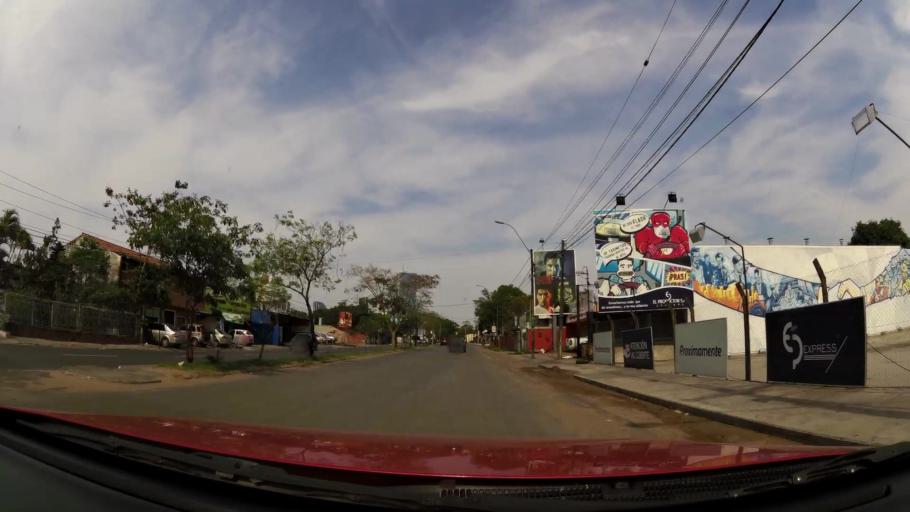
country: PY
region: Central
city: Fernando de la Mora
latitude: -25.2768
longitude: -57.5507
